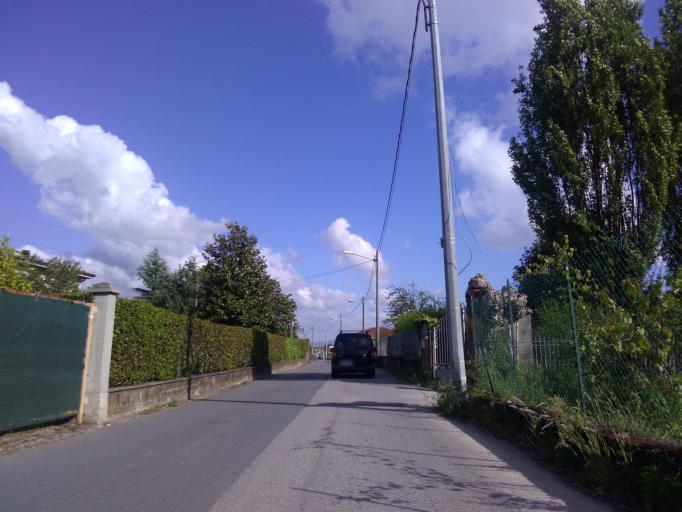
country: IT
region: Tuscany
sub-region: Provincia di Massa-Carrara
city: Massa
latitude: 44.0122
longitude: 10.1373
